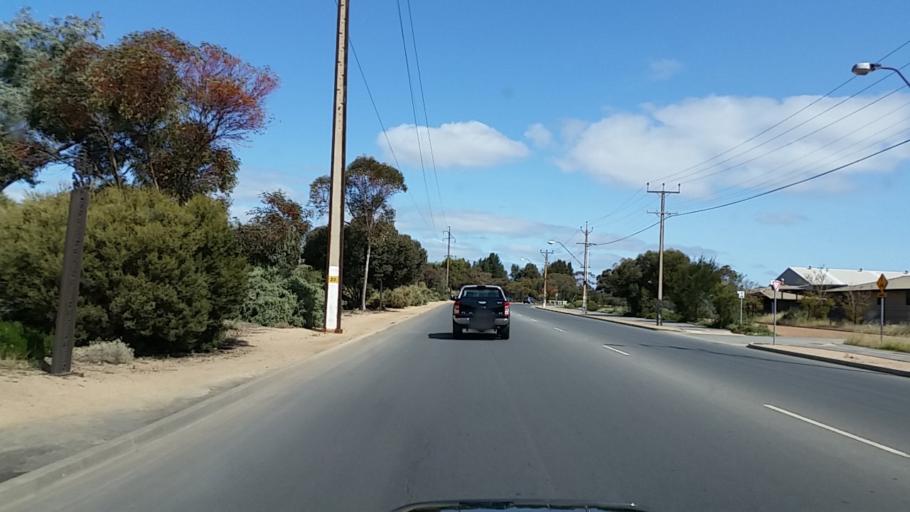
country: AU
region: South Australia
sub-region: Port Pirie City and Dists
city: Port Pirie
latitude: -33.1857
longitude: 138.0116
